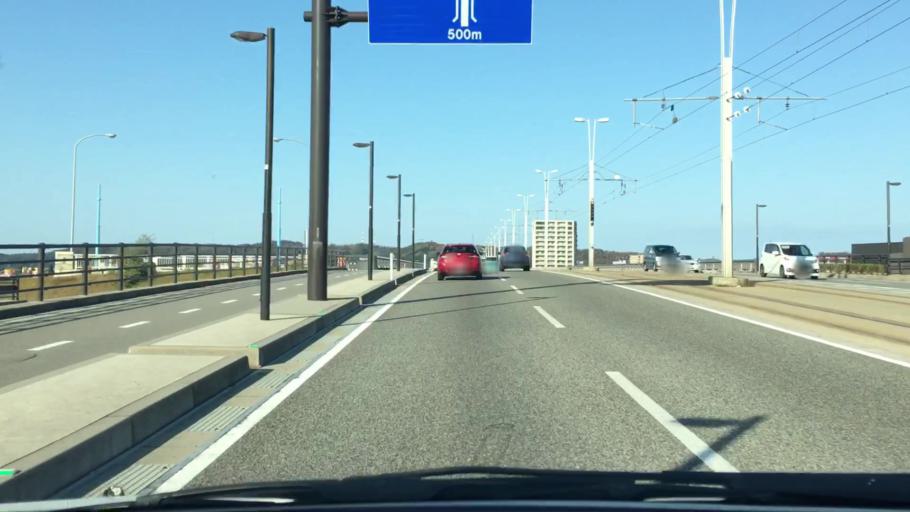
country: JP
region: Toyama
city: Toyama-shi
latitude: 36.6929
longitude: 137.2022
